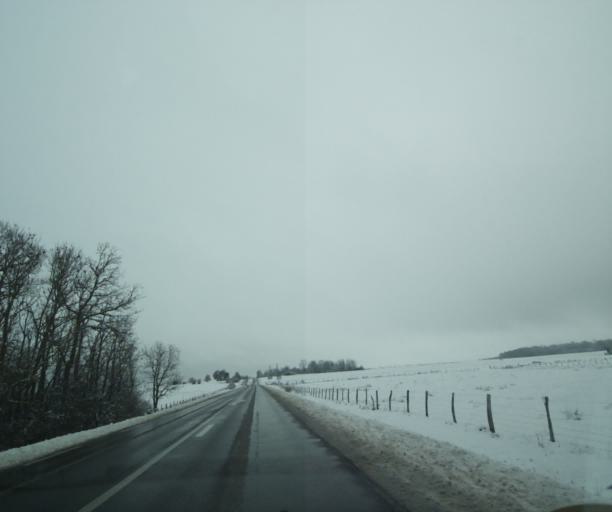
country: FR
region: Champagne-Ardenne
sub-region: Departement de la Haute-Marne
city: Montier-en-Der
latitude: 48.5261
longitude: 4.8139
